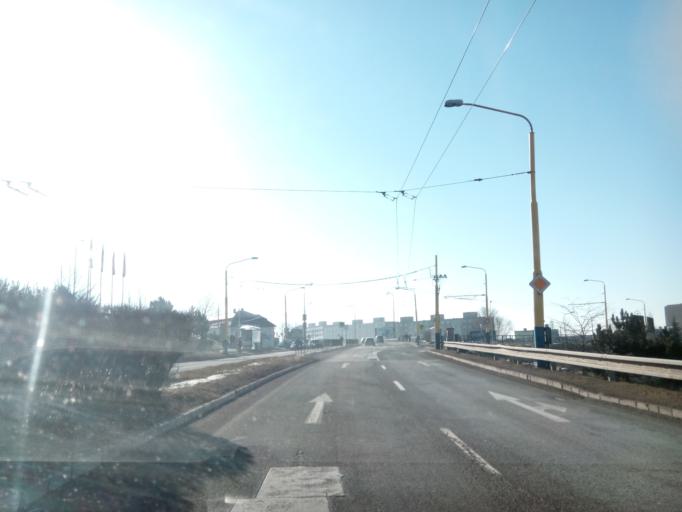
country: SK
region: Kosicky
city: Kosice
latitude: 48.7314
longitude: 21.2898
